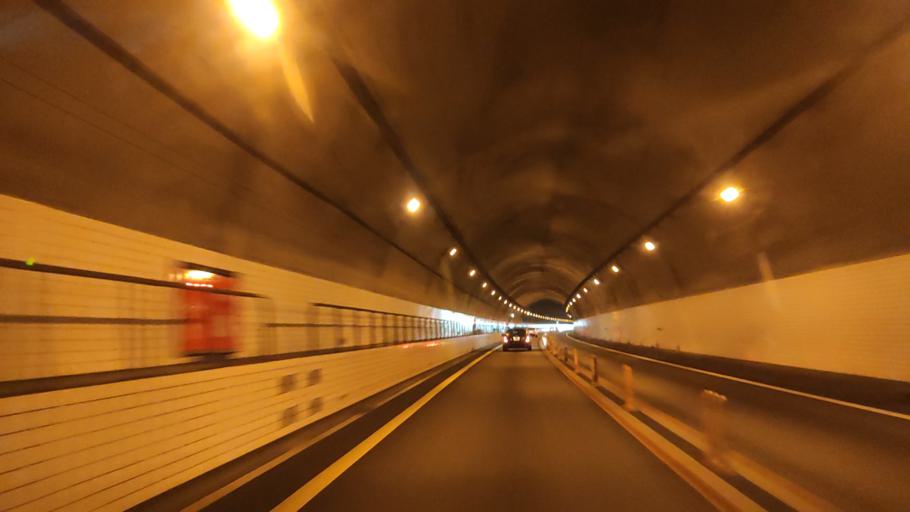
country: JP
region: Tokushima
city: Ikedacho
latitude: 34.0206
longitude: 133.8088
